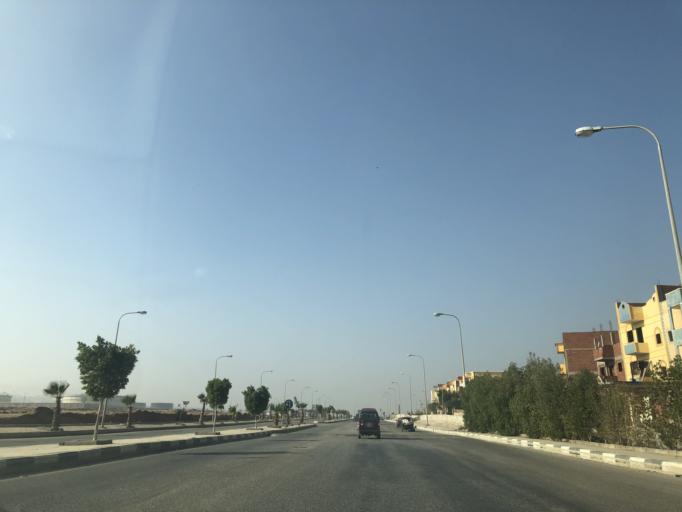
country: EG
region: Al Jizah
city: Madinat Sittah Uktubar
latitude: 29.9307
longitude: 31.0468
